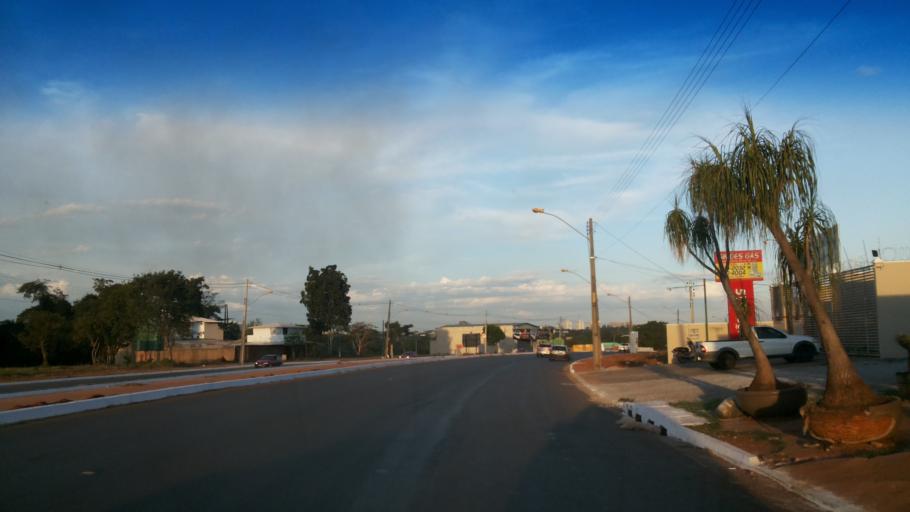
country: BR
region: Goias
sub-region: Goiania
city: Goiania
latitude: -16.6230
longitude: -49.2766
